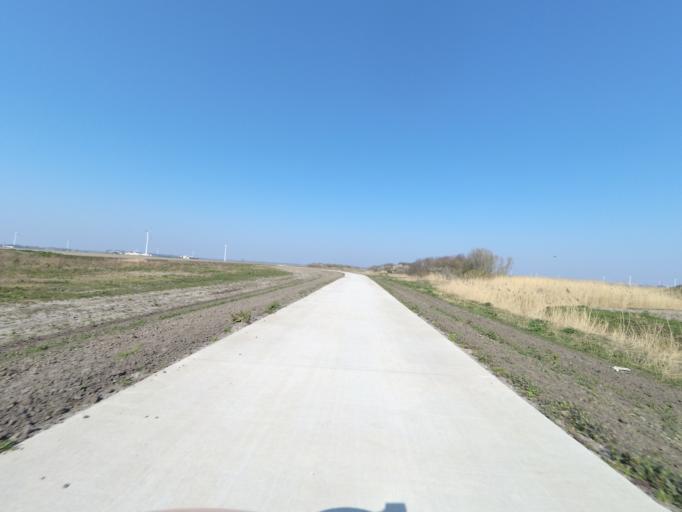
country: NL
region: Utrecht
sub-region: Gemeente Bunschoten
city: Spakenburg
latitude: 52.3717
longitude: 5.3754
